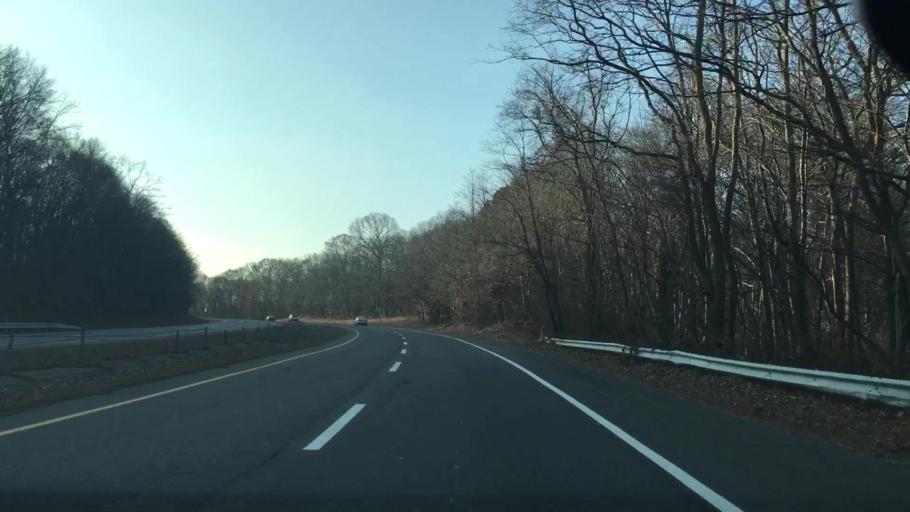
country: US
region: New York
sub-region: Suffolk County
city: Setauket-East Setauket
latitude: 40.9104
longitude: -73.1186
